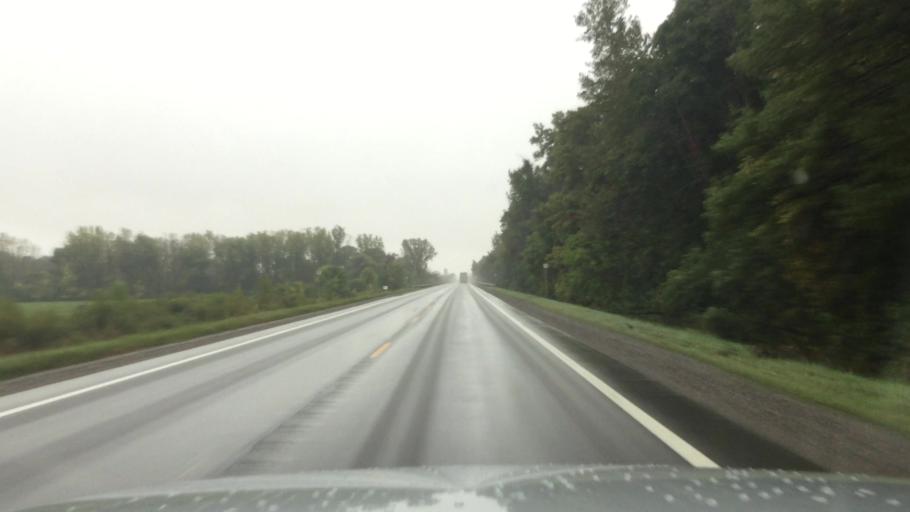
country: US
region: Michigan
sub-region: Saginaw County
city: Saginaw
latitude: 43.3708
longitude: -83.9551
